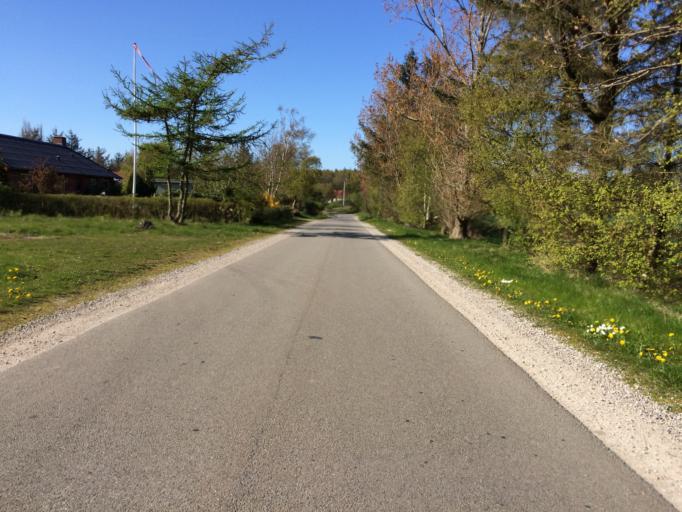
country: DK
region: Central Jutland
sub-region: Struer Kommune
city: Struer
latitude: 56.5481
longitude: 8.6240
